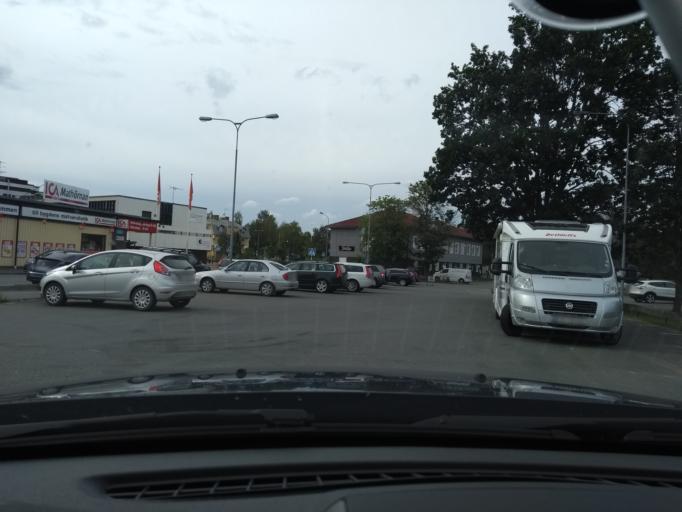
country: SE
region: Joenkoeping
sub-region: Eksjo Kommun
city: Mariannelund
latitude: 57.6159
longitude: 15.5730
